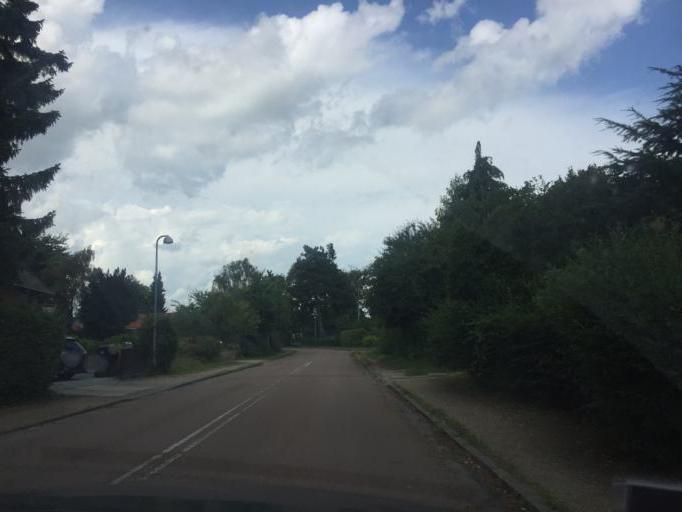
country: DK
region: Capital Region
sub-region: Rudersdal Kommune
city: Holte
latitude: 55.7916
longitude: 12.4520
